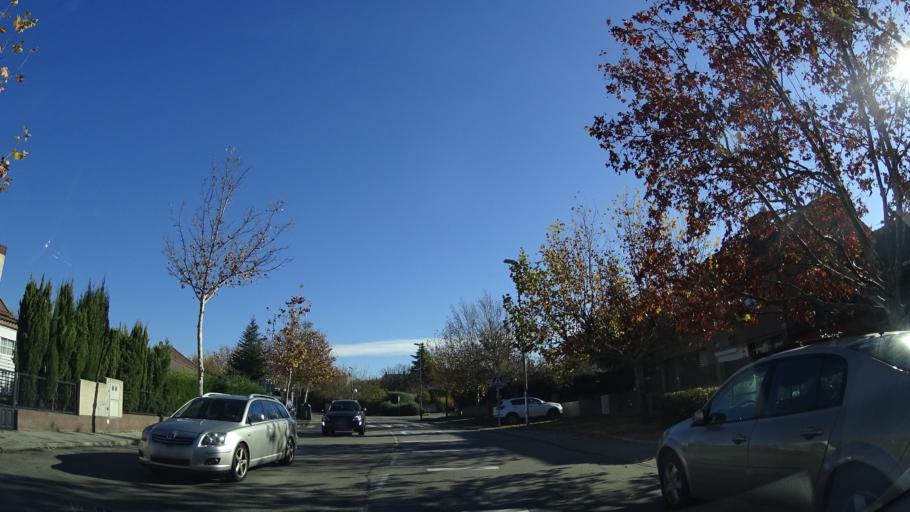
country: ES
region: Madrid
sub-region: Provincia de Madrid
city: Las Matas
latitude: 40.5208
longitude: -3.9102
